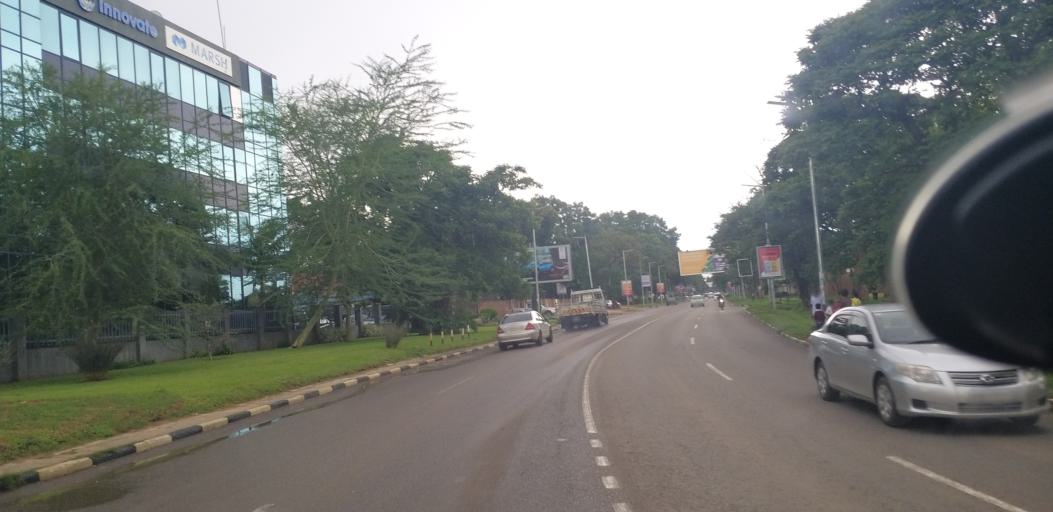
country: ZM
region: Lusaka
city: Lusaka
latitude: -15.4154
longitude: 28.2960
